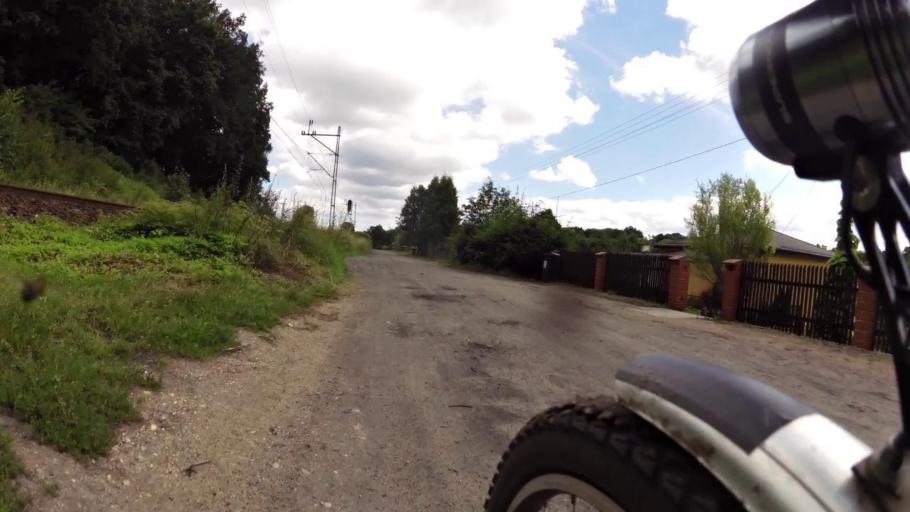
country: PL
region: West Pomeranian Voivodeship
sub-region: Powiat swidwinski
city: Rabino
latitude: 53.8651
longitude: 15.9462
